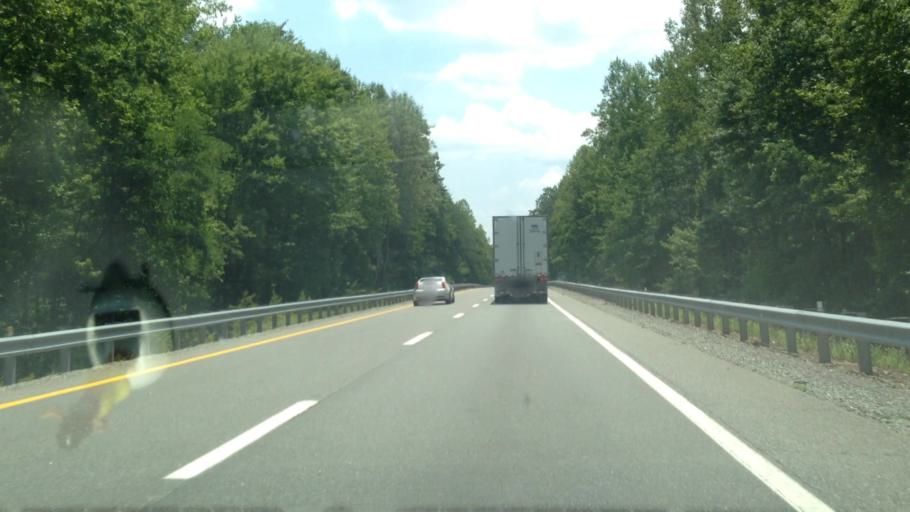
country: US
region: Virginia
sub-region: Henry County
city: Horse Pasture
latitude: 36.6393
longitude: -79.8955
